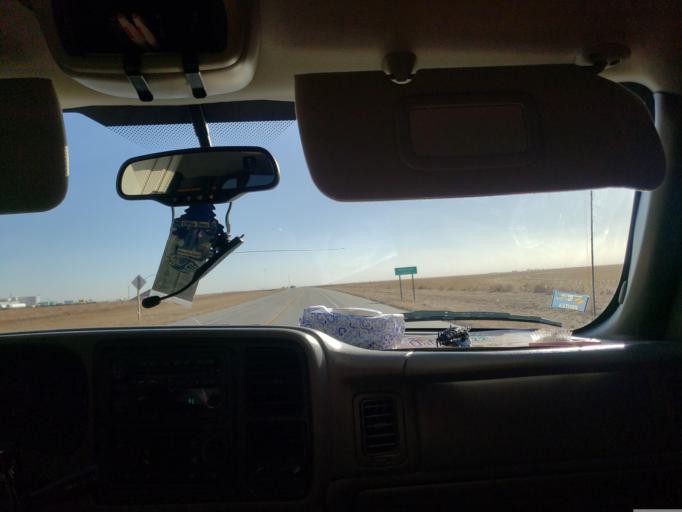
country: US
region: Kansas
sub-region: Finney County
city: Garden City
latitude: 37.7724
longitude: -100.8714
